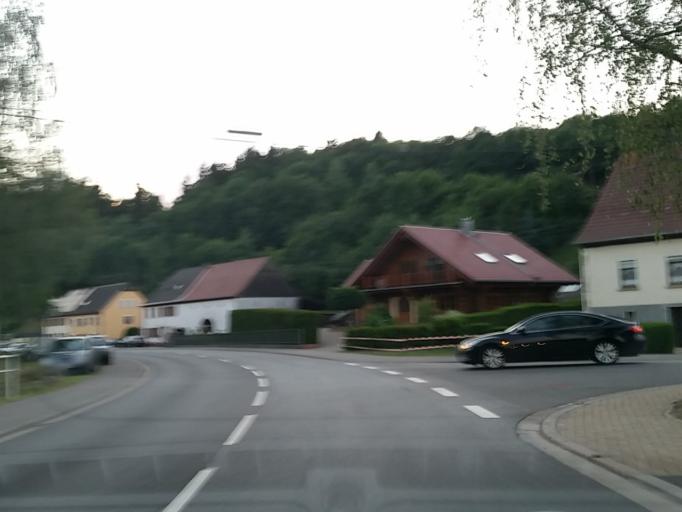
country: DE
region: Saarland
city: Wadern
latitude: 49.5273
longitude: 6.9373
